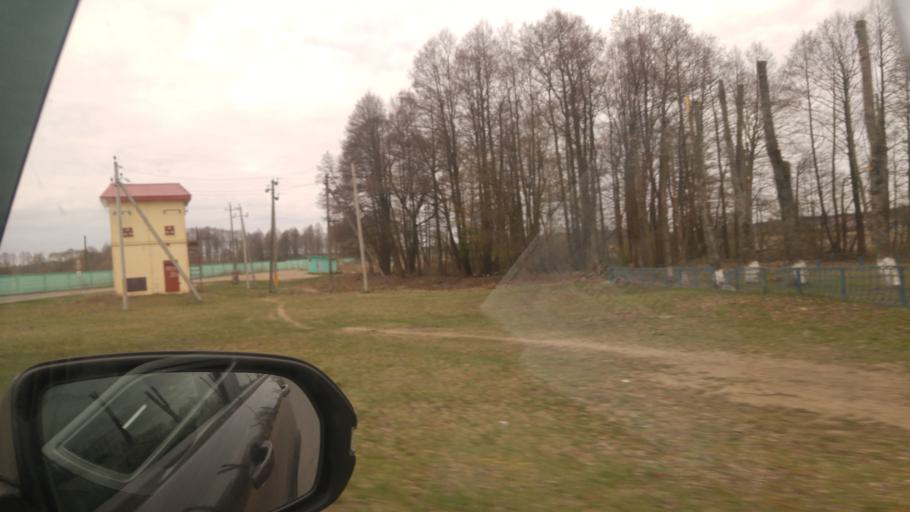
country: BY
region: Minsk
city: Smilavichy
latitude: 53.7204
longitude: 28.1423
